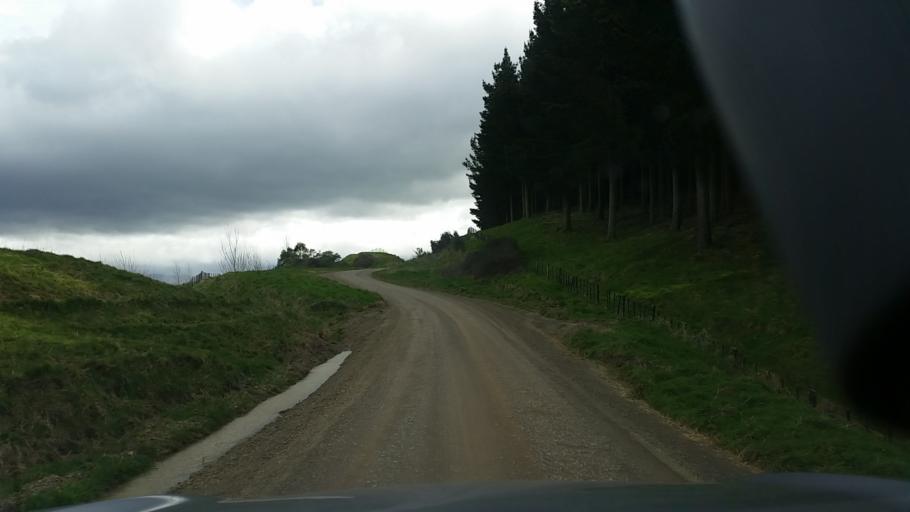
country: NZ
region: Hawke's Bay
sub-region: Napier City
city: Napier
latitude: -39.2042
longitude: 176.9180
